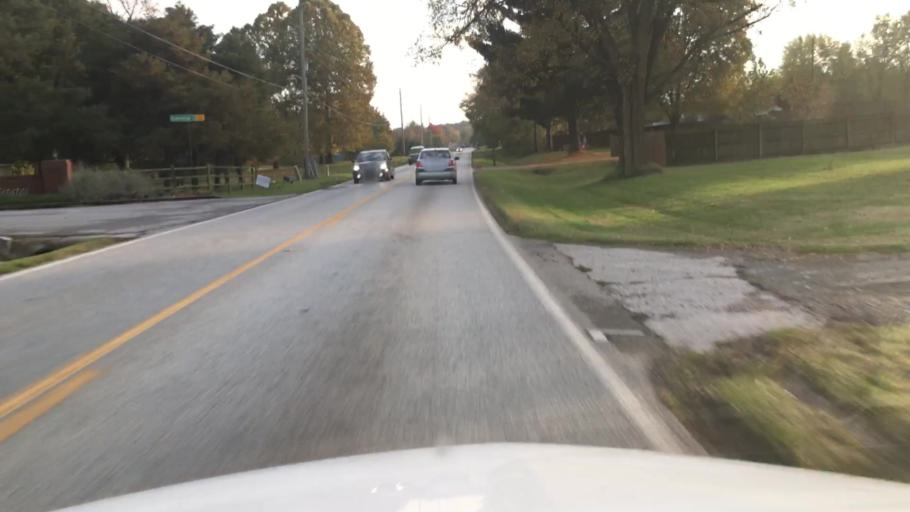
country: US
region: Arkansas
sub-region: Washington County
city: Elm Springs
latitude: 36.2168
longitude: -94.2309
